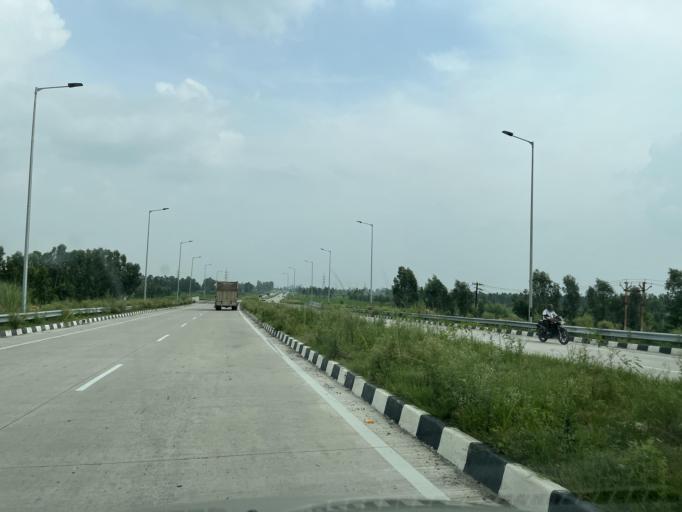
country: IN
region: Uttarakhand
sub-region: Udham Singh Nagar
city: Kashipur
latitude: 29.1720
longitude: 78.9499
